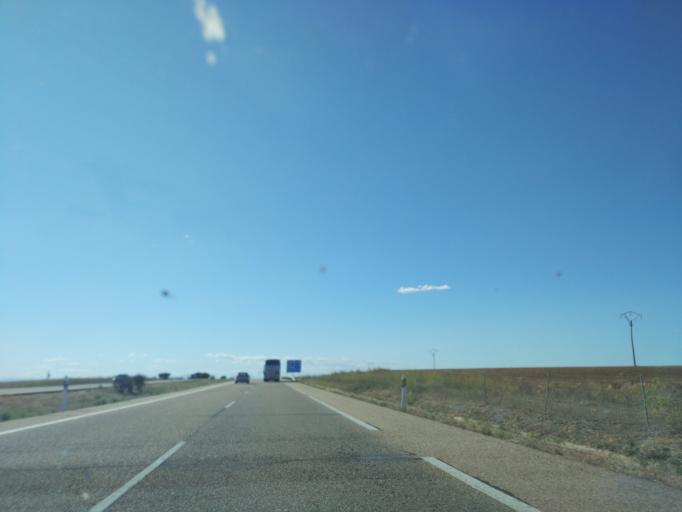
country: ES
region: Castille and Leon
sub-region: Provincia de Zamora
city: San Esteban del Molar
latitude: 41.9564
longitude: -5.5758
